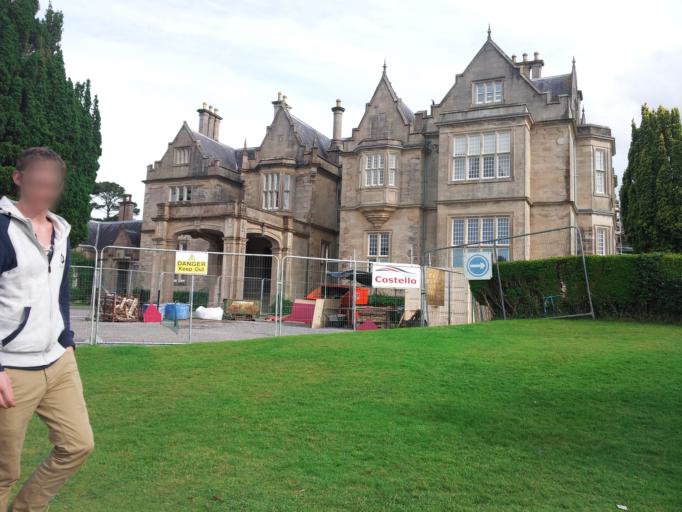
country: IE
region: Munster
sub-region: Ciarrai
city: Cill Airne
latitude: 52.0184
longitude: -9.5047
